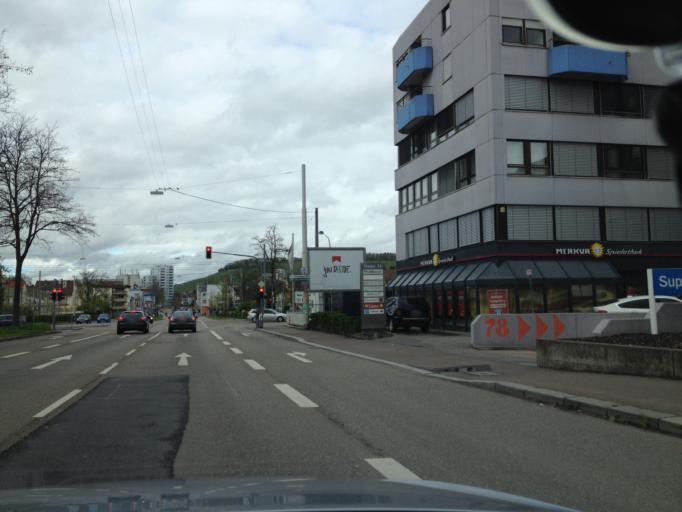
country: DE
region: Baden-Wuerttemberg
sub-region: Regierungsbezirk Stuttgart
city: Heilbronn
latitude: 49.1406
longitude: 9.2297
